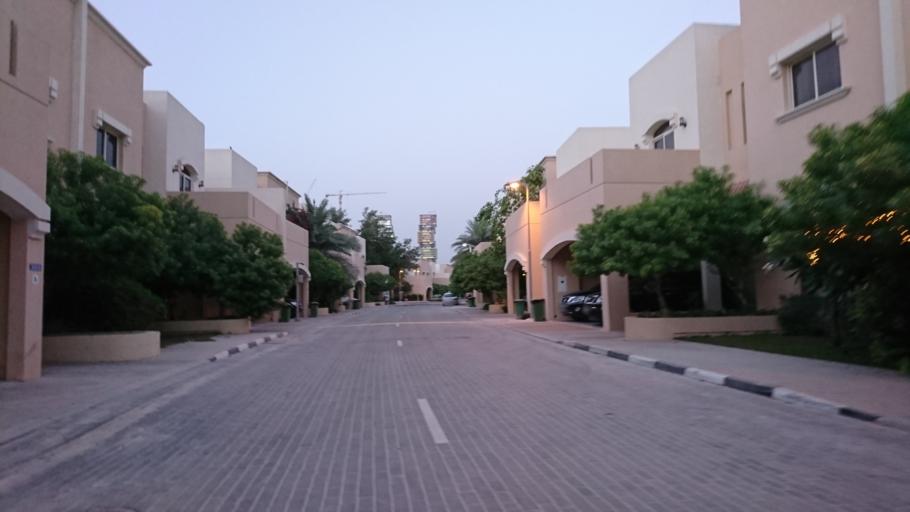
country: QA
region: Baladiyat ad Dawhah
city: Doha
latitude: 25.3840
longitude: 51.5143
